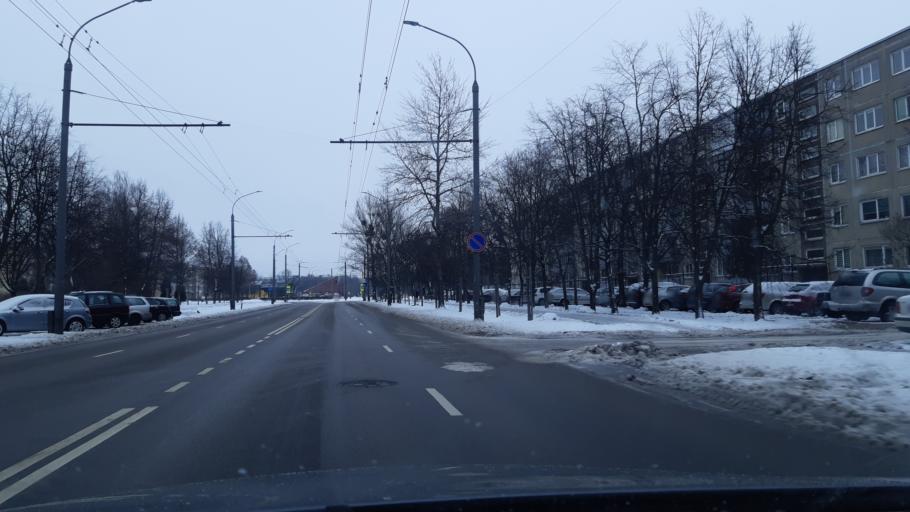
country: LT
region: Kauno apskritis
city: Dainava (Kaunas)
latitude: 54.9218
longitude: 23.9769
